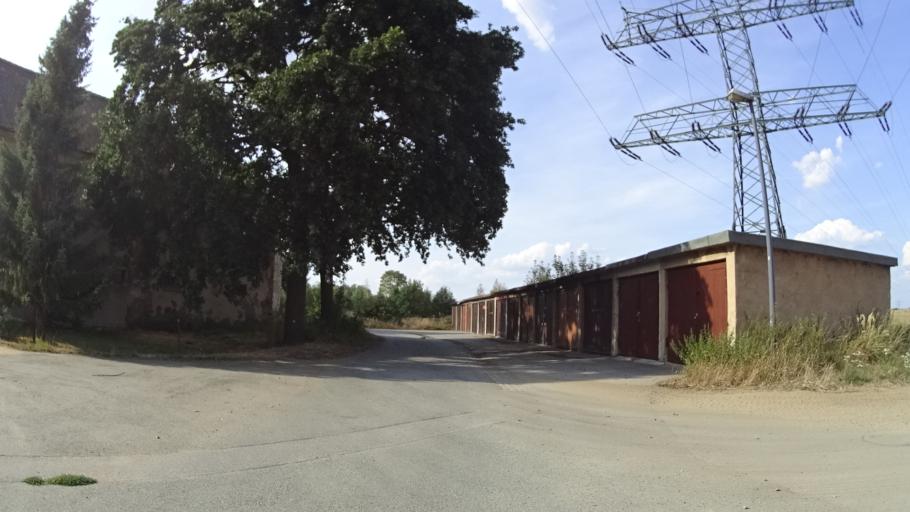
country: DE
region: Saxony
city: Ostritz
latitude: 51.0730
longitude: 14.9674
